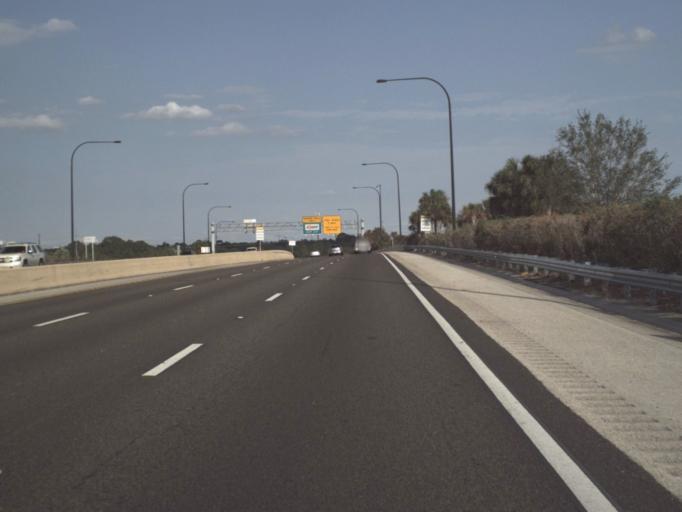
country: US
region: Florida
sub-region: Orange County
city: Pine Hills
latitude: 28.5495
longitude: -81.4588
